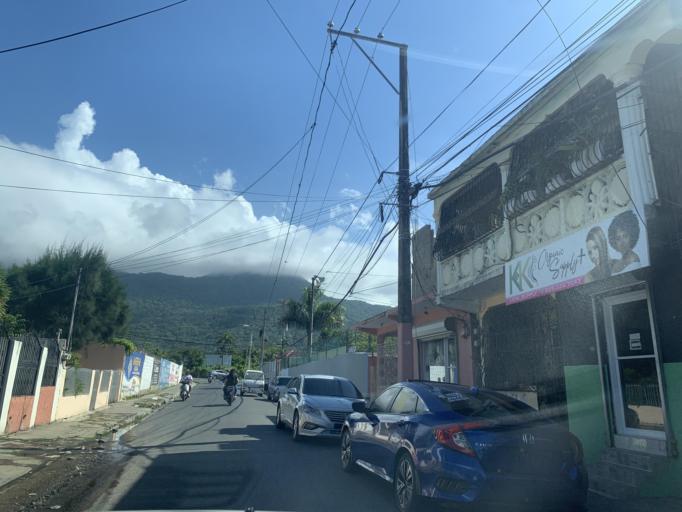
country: DO
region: Puerto Plata
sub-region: Puerto Plata
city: Puerto Plata
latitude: 19.7922
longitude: -70.6949
